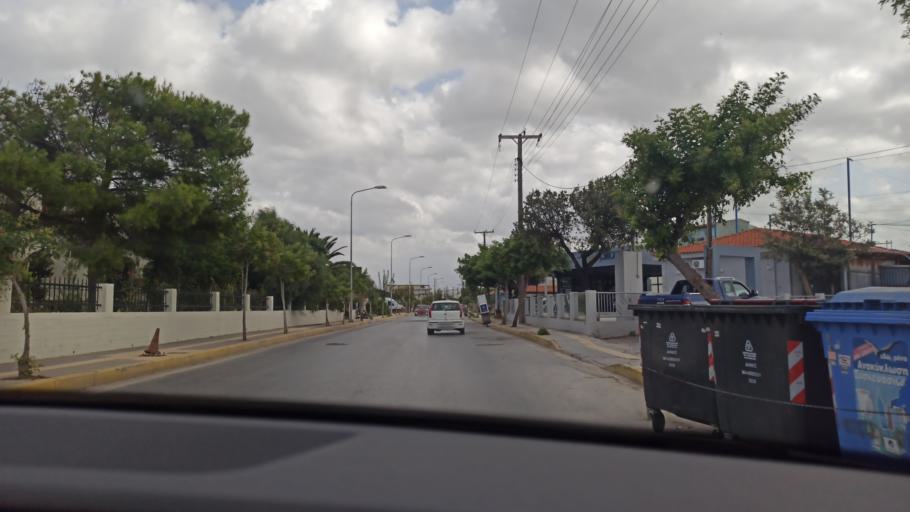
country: GR
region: Crete
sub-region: Nomos Irakleiou
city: Gazi
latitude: 35.3349
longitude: 25.0924
